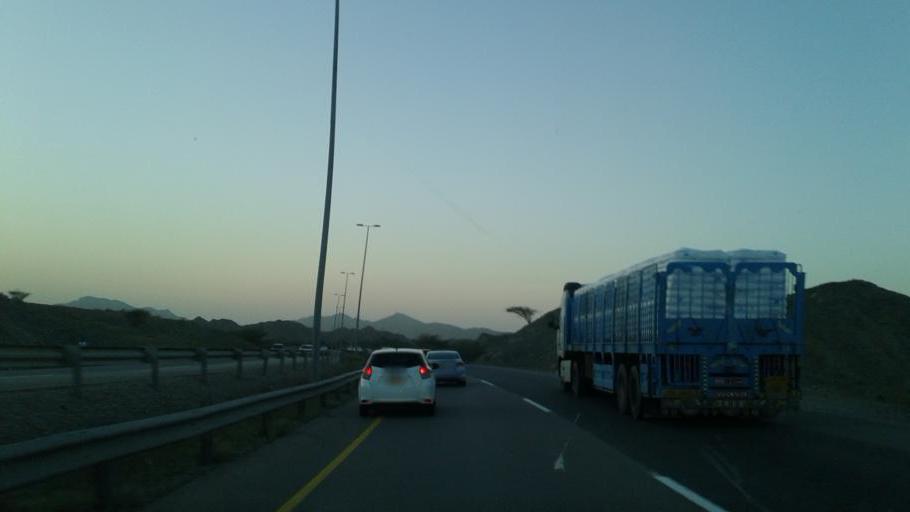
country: OM
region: Muhafazat ad Dakhiliyah
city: Bidbid
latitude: 23.5028
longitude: 58.1945
